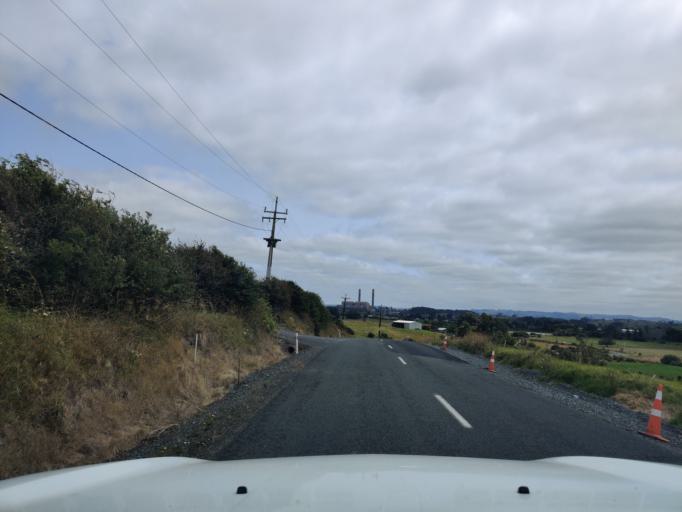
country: NZ
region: Waikato
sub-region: Waikato District
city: Te Kauwhata
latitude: -37.5244
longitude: 175.1737
